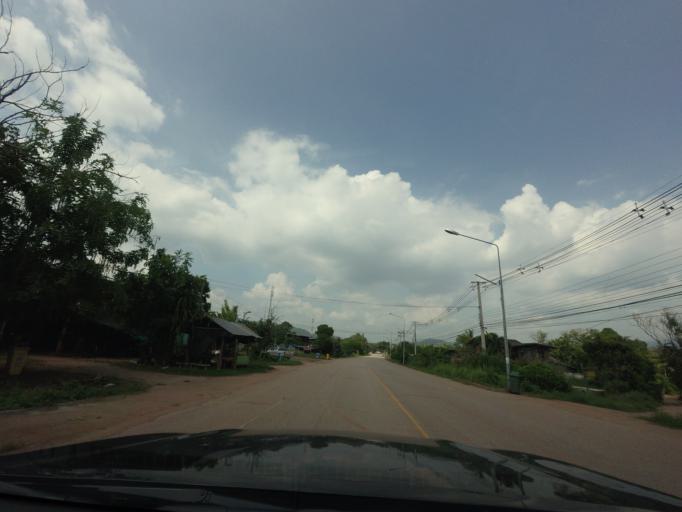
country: TH
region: Uttaradit
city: Ban Khok
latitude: 18.0236
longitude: 101.0726
